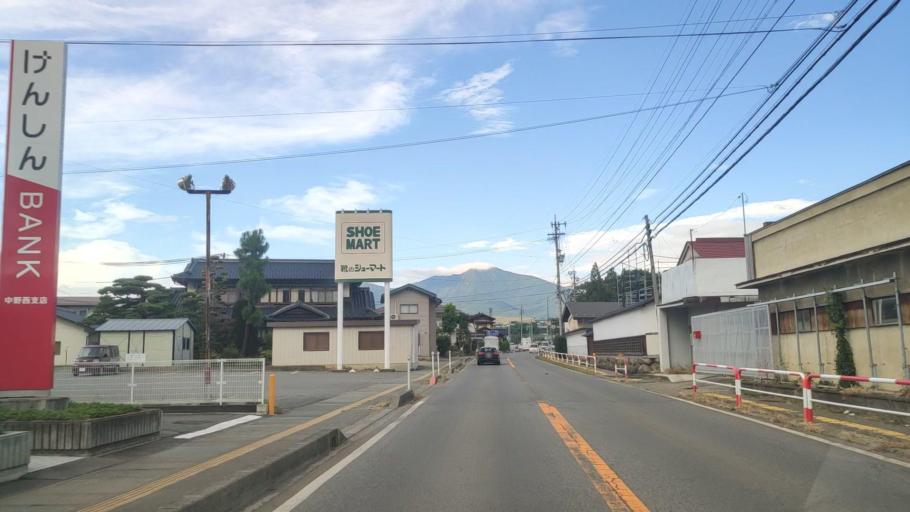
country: JP
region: Nagano
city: Nakano
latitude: 36.7408
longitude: 138.3485
